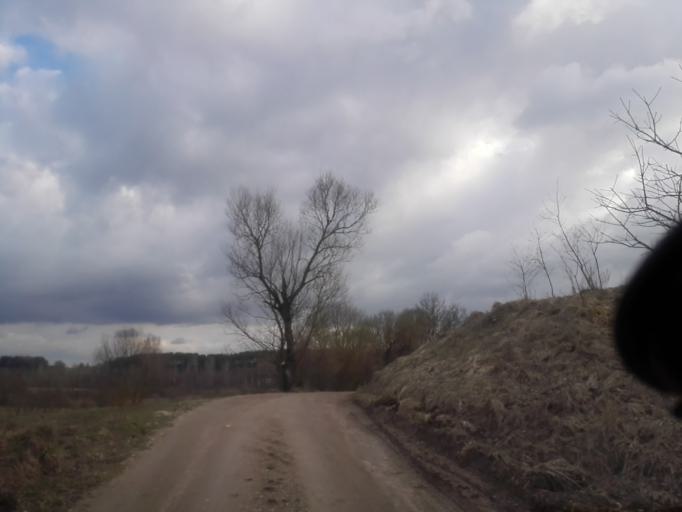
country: PL
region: Podlasie
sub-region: Suwalki
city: Suwalki
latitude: 54.2206
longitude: 22.8101
